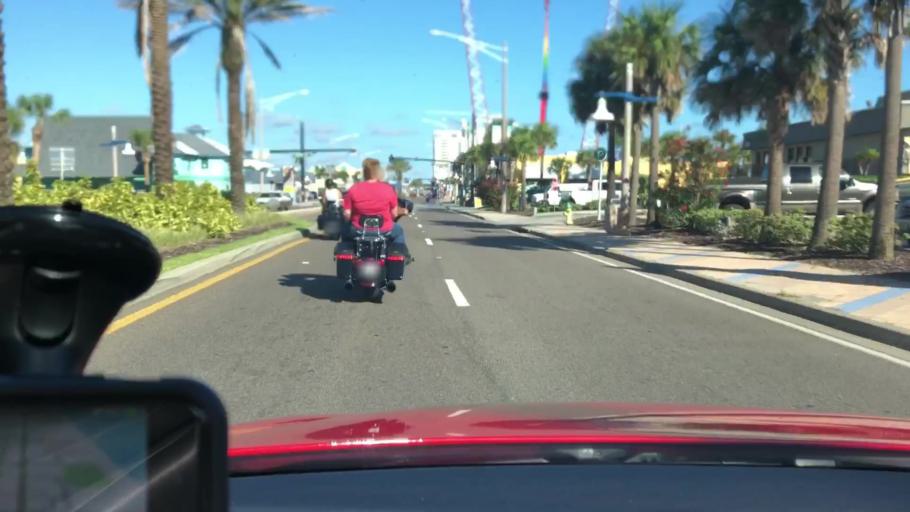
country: US
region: Florida
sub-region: Volusia County
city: Daytona Beach
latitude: 29.2242
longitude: -81.0069
